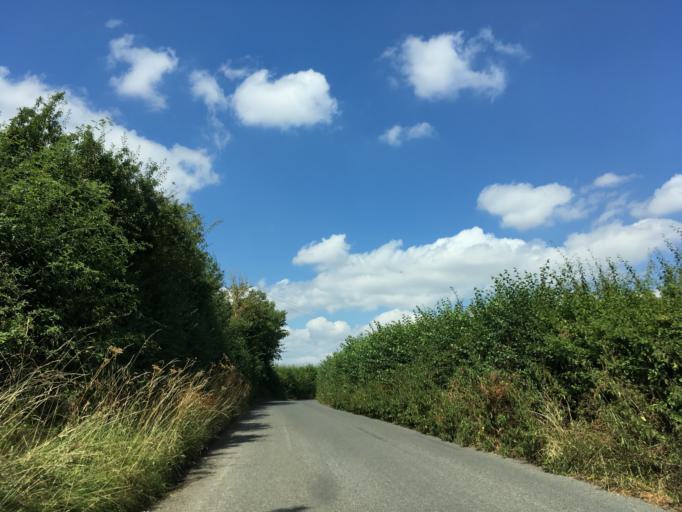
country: GB
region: England
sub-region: Gloucestershire
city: Shurdington
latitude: 51.8513
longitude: -2.1271
